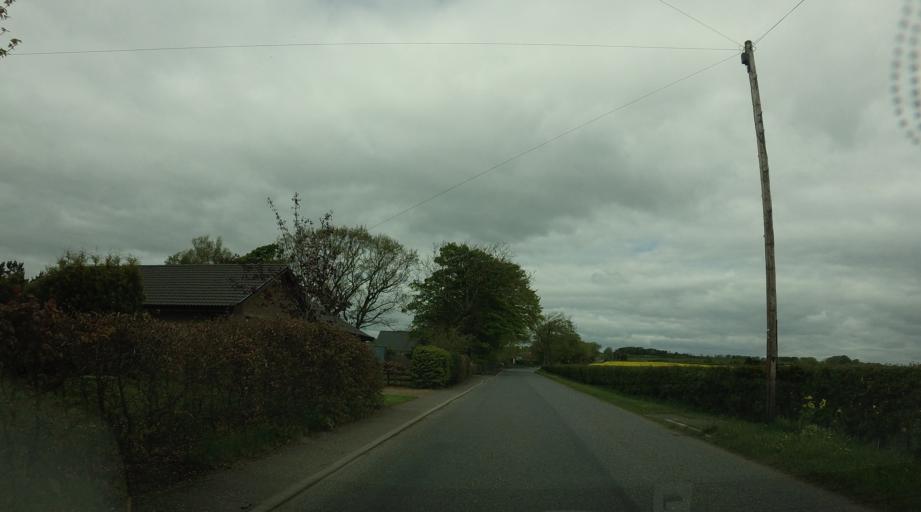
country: GB
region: Scotland
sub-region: Perth and Kinross
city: Milnathort
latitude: 56.2410
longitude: -3.3709
